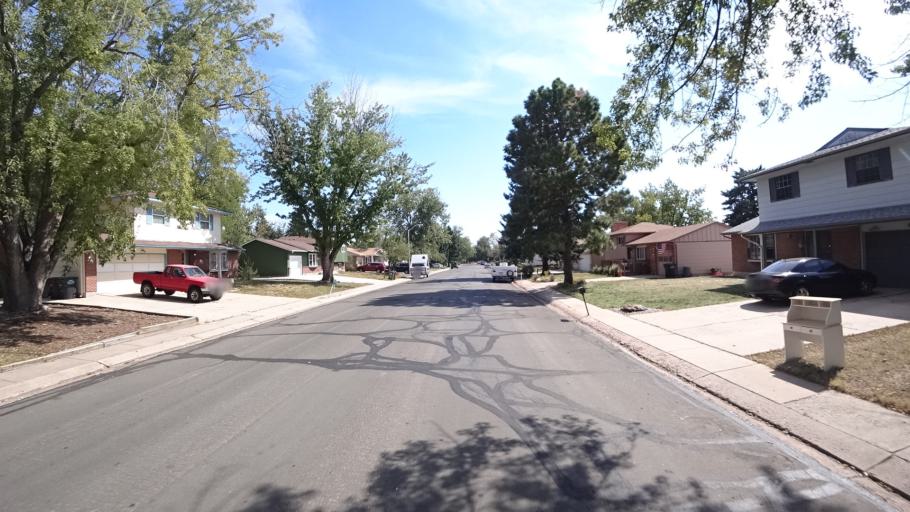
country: US
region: Colorado
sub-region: El Paso County
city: Cimarron Hills
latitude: 38.8999
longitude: -104.7635
